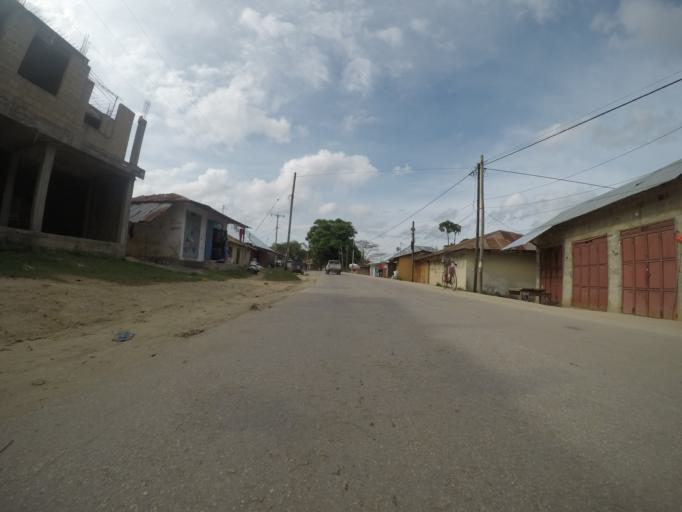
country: TZ
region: Pemba South
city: Chake Chake
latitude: -5.2373
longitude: 39.7797
